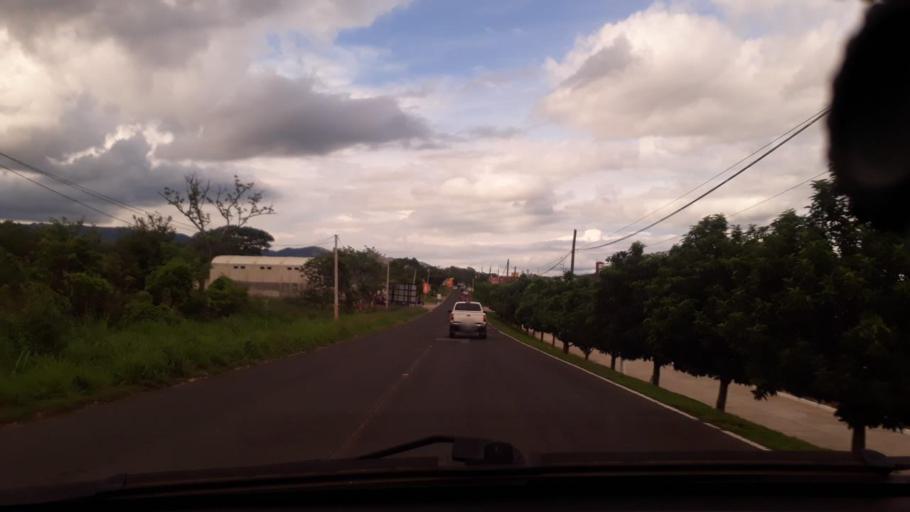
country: GT
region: Jutiapa
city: Jutiapa
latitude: 14.2802
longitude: -89.9585
